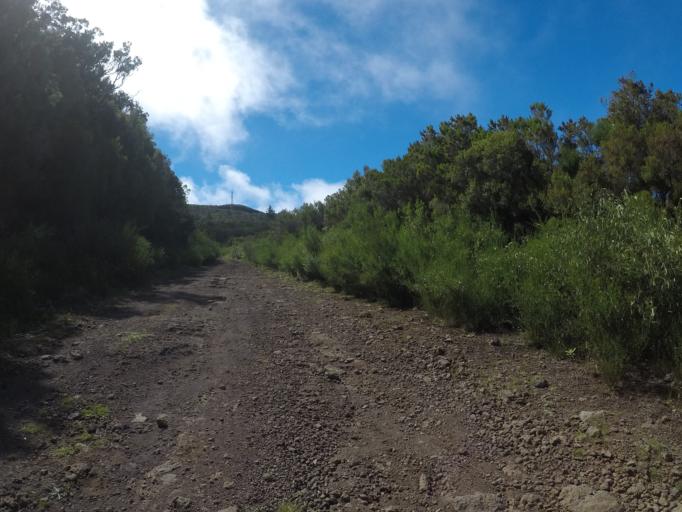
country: PT
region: Madeira
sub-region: Sao Vicente
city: Sao Vicente
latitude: 32.7719
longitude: -17.0602
